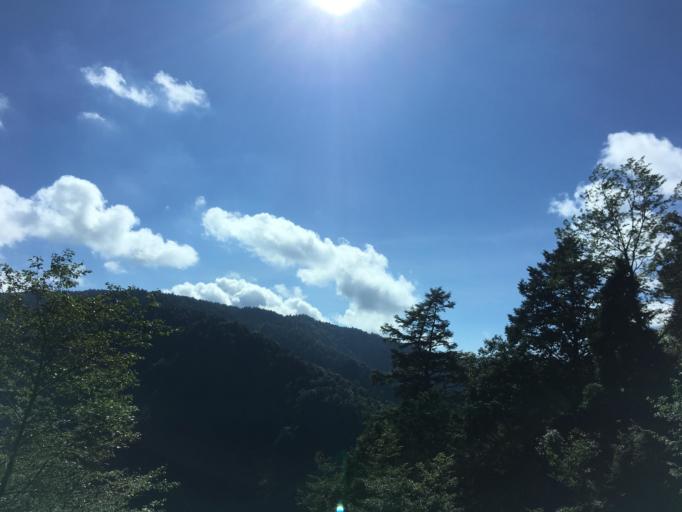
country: TW
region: Taiwan
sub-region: Yilan
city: Yilan
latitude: 24.5113
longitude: 121.5682
